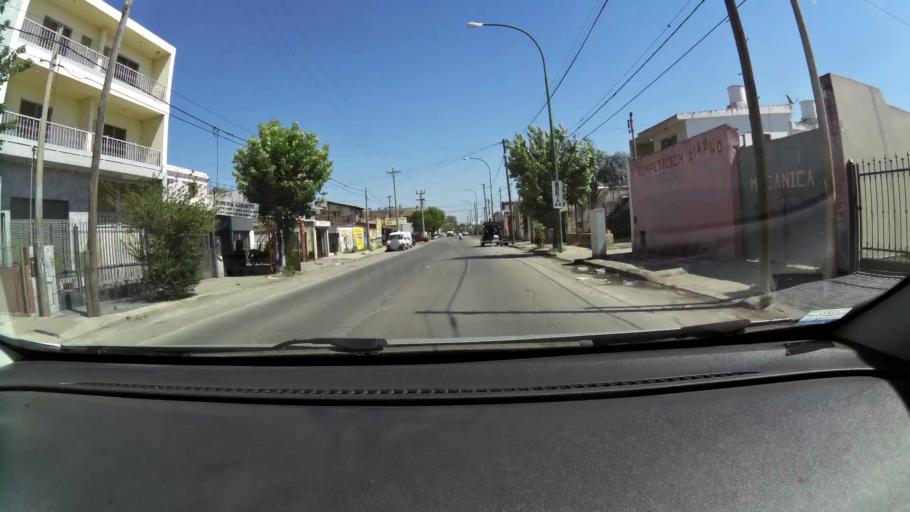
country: AR
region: Cordoba
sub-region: Departamento de Capital
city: Cordoba
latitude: -31.3749
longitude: -64.1478
